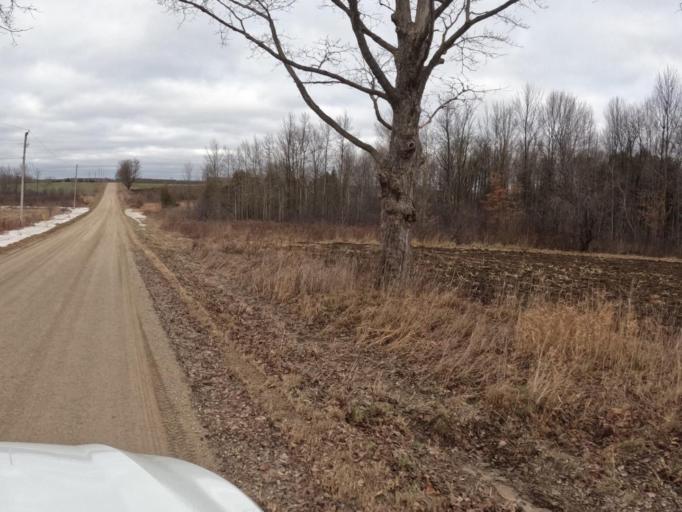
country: CA
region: Ontario
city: Shelburne
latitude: 43.8883
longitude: -80.4059
